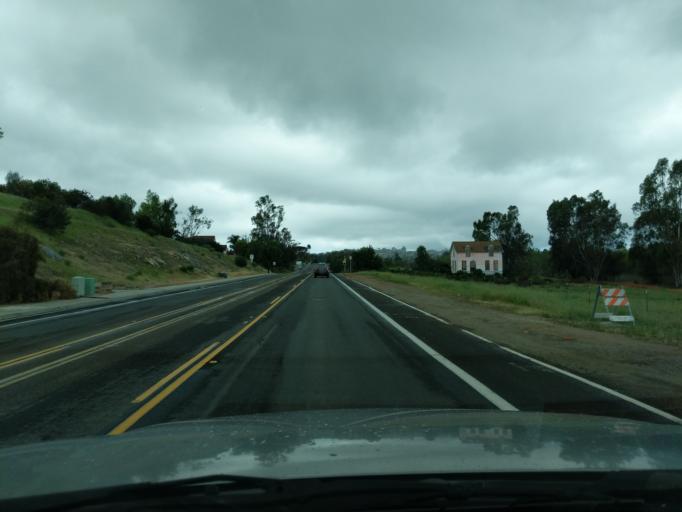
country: US
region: California
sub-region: San Diego County
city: Lake San Marcos
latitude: 33.1304
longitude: -117.1881
